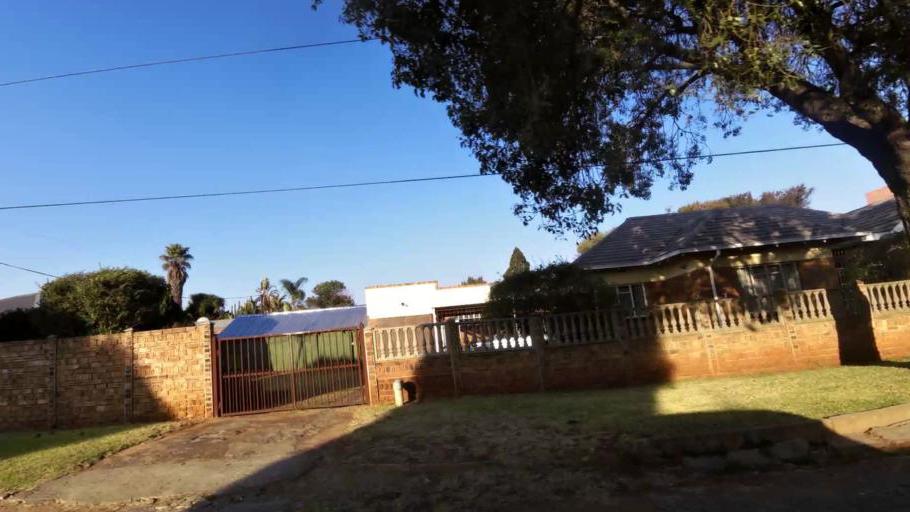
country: ZA
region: Gauteng
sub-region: City of Johannesburg Metropolitan Municipality
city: Roodepoort
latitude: -26.1708
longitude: 27.9466
